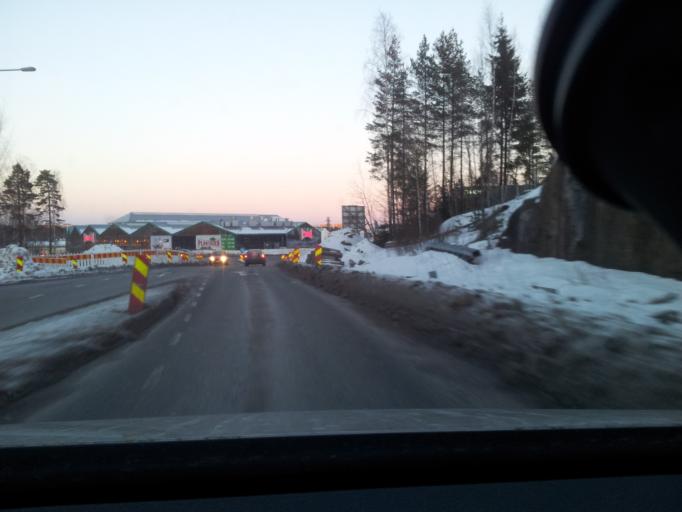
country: FI
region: Uusimaa
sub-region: Helsinki
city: Kauniainen
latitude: 60.1579
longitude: 24.7054
